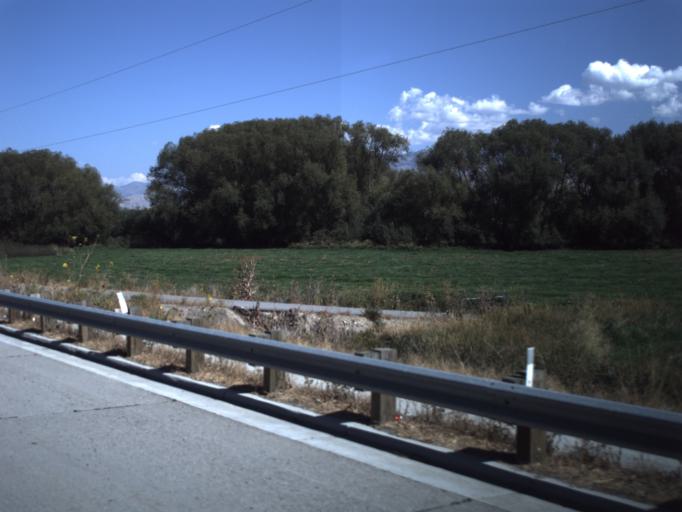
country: US
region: Utah
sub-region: Cache County
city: Logan
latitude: 41.7066
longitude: -111.8604
